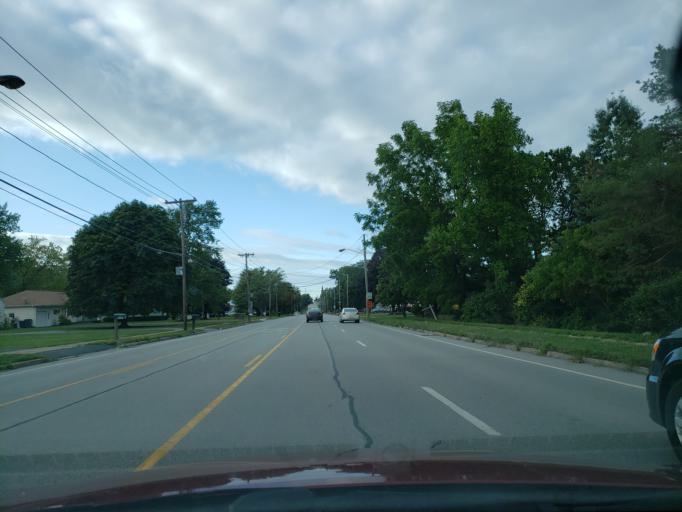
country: US
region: New York
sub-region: Monroe County
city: Greece
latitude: 43.2436
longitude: -77.6591
